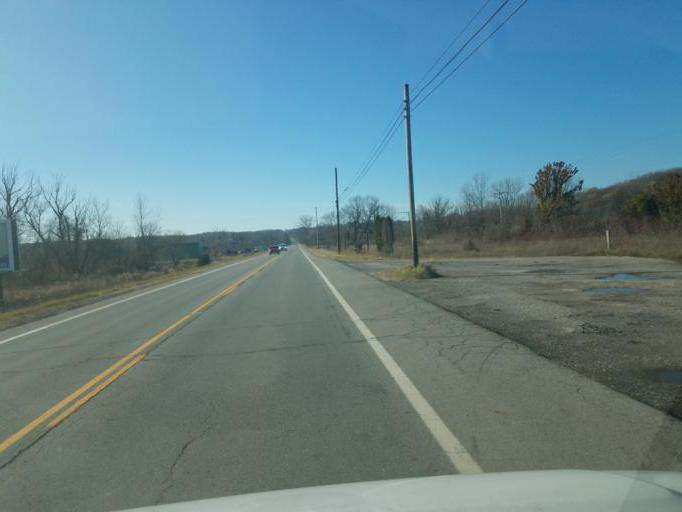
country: US
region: Ohio
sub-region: Richland County
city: Lincoln Heights
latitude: 40.8097
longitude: -82.4187
